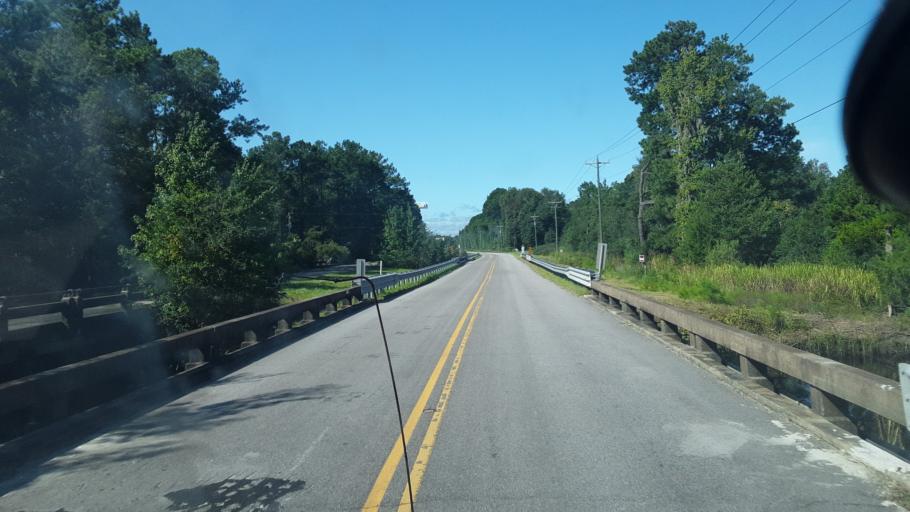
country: US
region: South Carolina
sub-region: Hampton County
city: Yemassee
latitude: 32.6017
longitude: -80.9025
